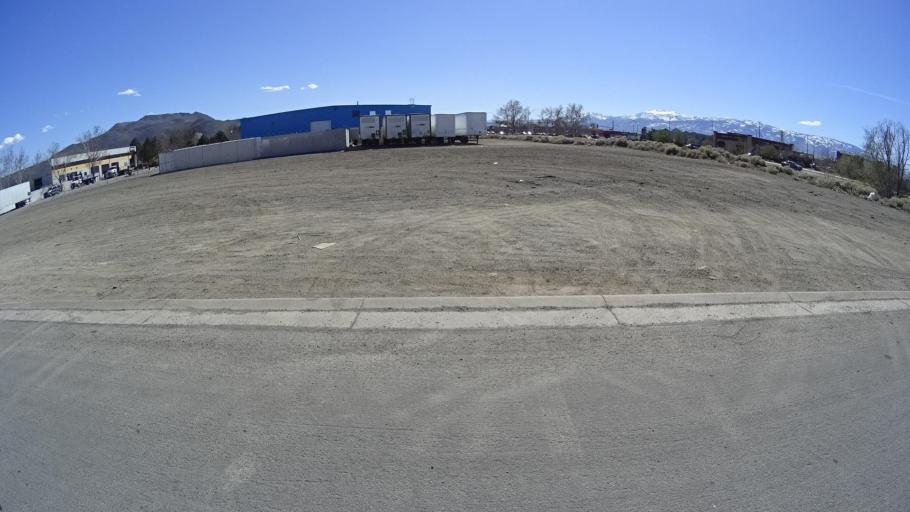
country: US
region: Nevada
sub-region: Washoe County
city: Sparks
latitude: 39.5353
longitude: -119.7144
